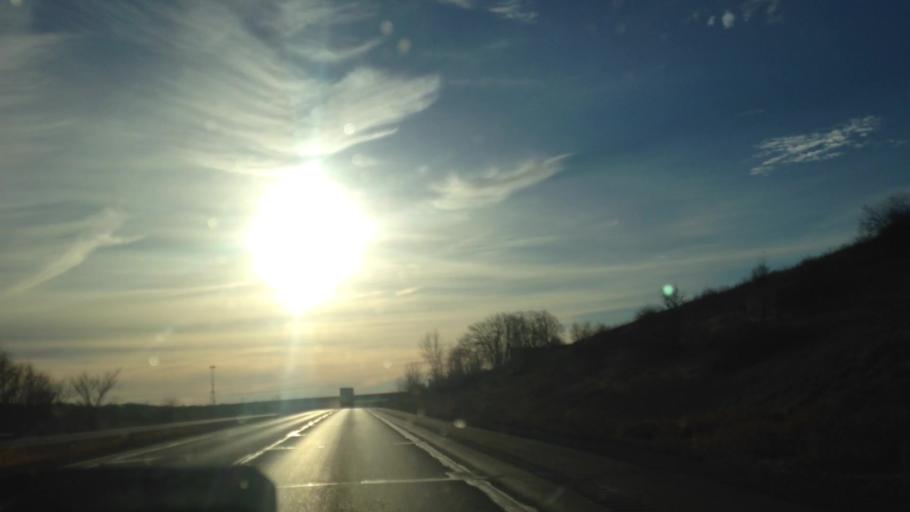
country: US
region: Wisconsin
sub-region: Dodge County
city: Theresa
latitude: 43.5186
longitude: -88.3808
